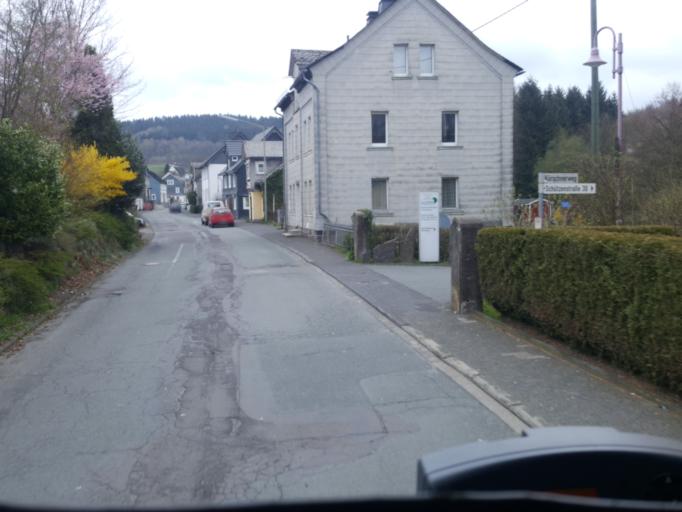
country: DE
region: North Rhine-Westphalia
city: Hilchenbach
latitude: 50.9982
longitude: 8.1078
